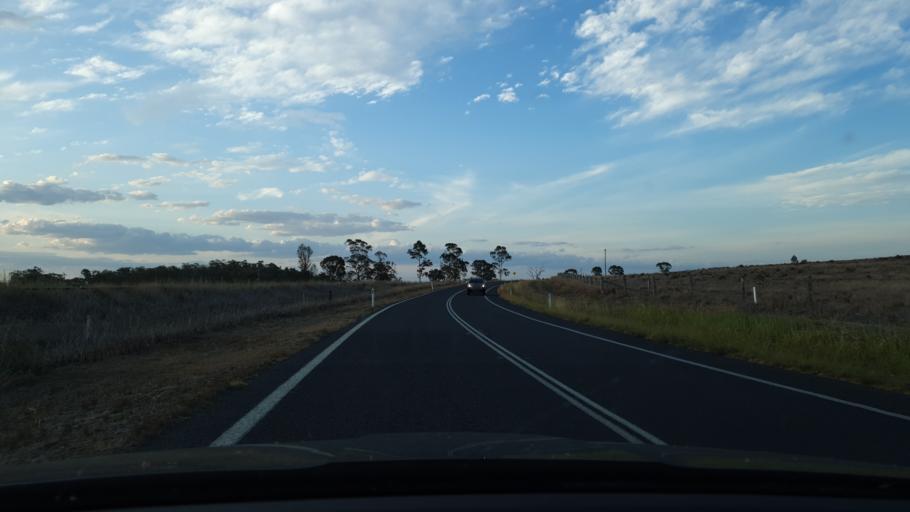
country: AU
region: Queensland
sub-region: Southern Downs
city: Warwick
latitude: -28.1788
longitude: 151.9751
